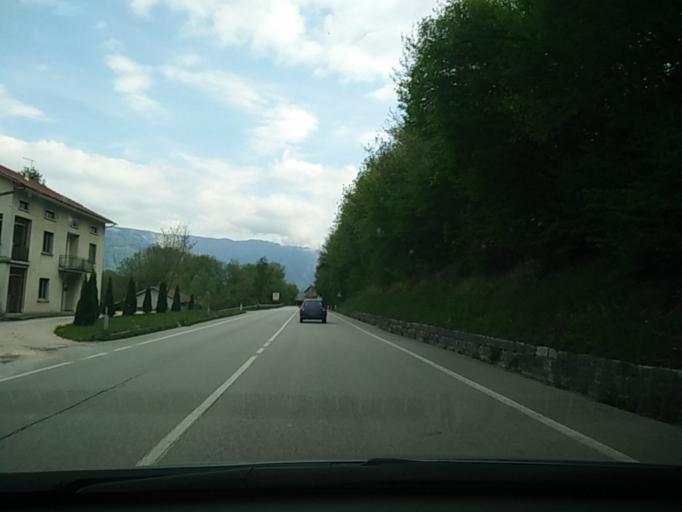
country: IT
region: Veneto
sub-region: Provincia di Belluno
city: Soccher-Paiane-Casan-Arsie
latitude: 46.1475
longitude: 12.3191
